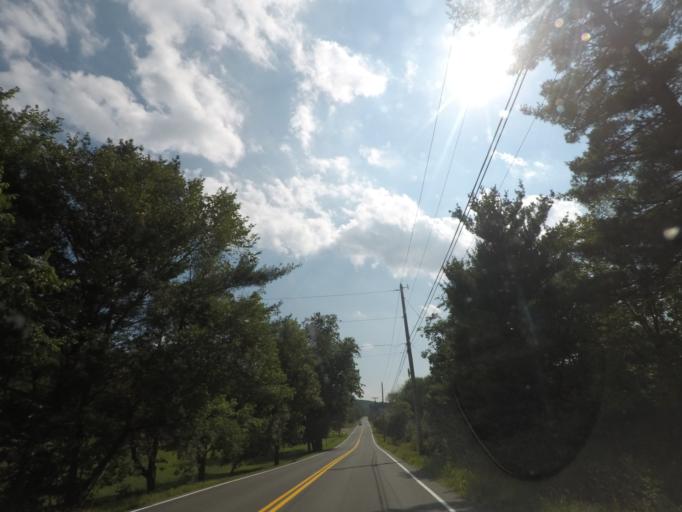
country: US
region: New York
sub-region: Rensselaer County
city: Poestenkill
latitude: 42.7859
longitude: -73.5339
